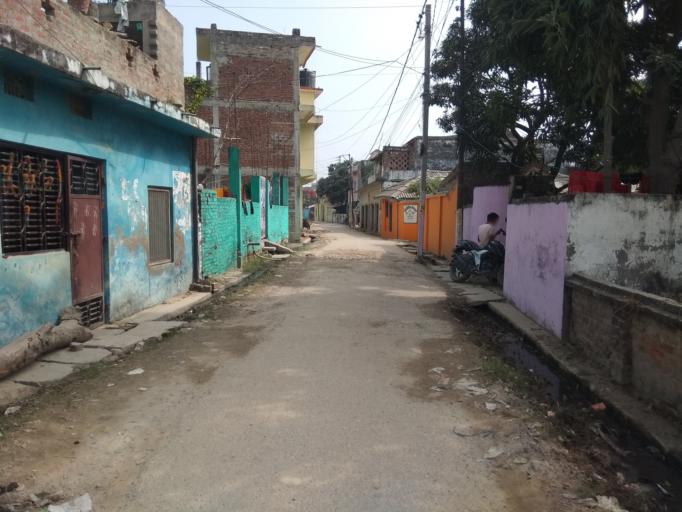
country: NP
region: Central Region
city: Janakpur
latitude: 26.7361
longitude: 85.9269
